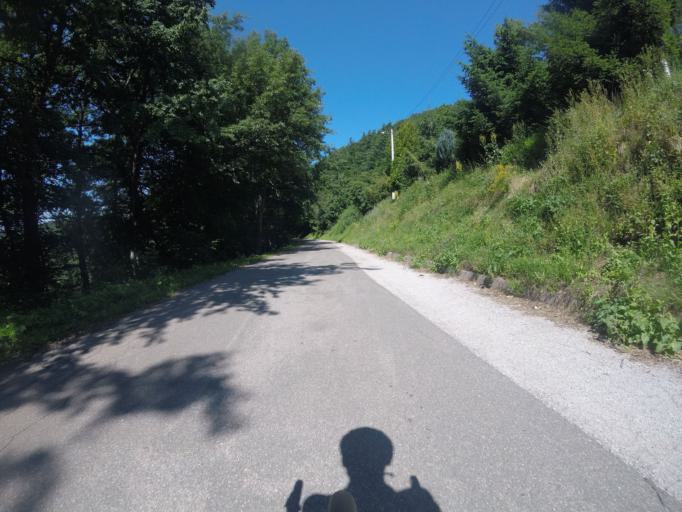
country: SI
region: Brezice
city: Brezice
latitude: 45.8192
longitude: 15.5285
